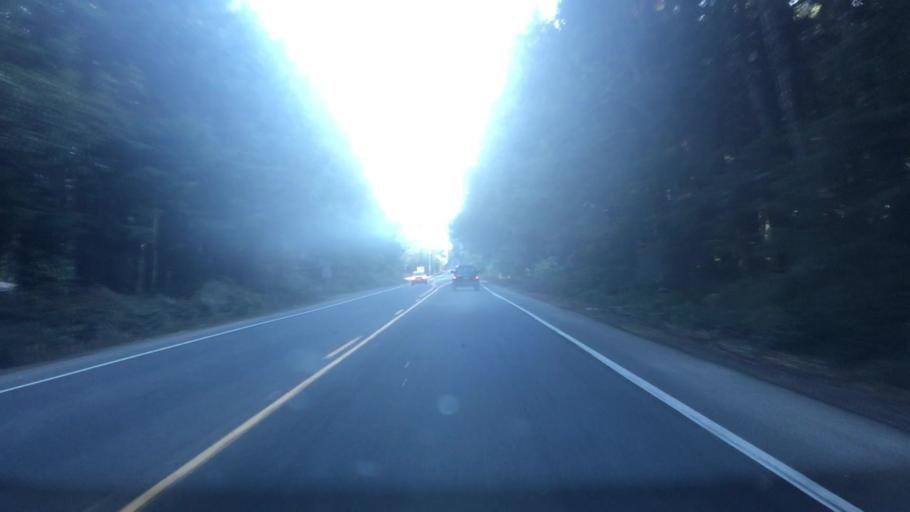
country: US
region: Oregon
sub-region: Clatsop County
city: Cannon Beach
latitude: 45.8907
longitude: -123.9571
